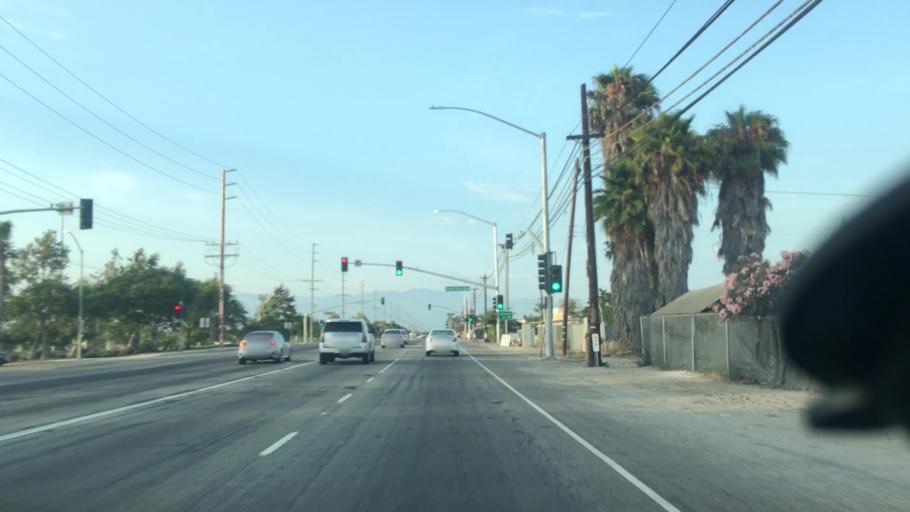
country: US
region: California
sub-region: Ventura County
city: El Rio
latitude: 34.2397
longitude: -119.1673
